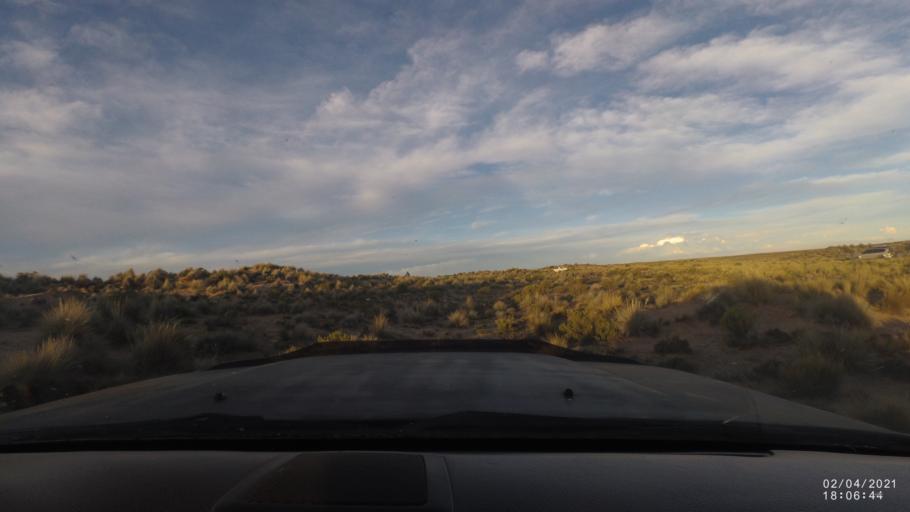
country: BO
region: Oruro
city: Poopo
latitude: -18.7099
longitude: -67.5402
